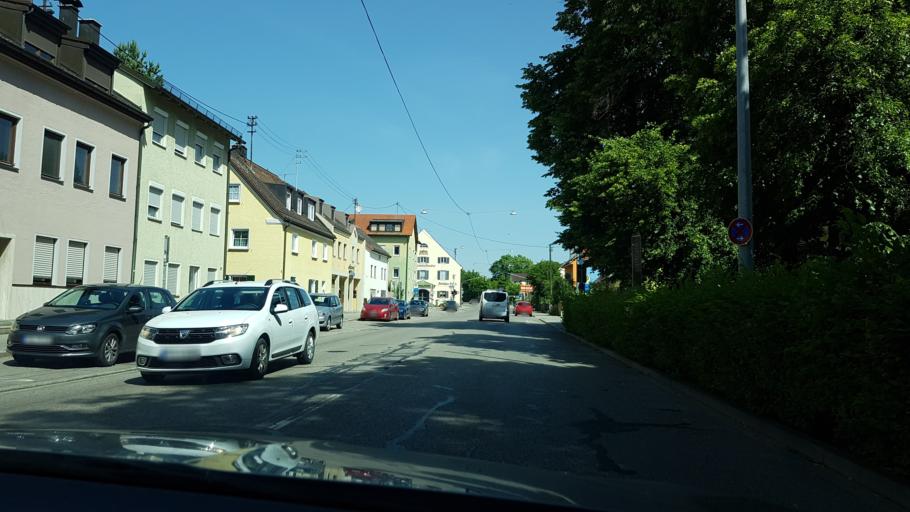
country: DE
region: Bavaria
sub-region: Upper Bavaria
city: Fuerstenfeldbruck
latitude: 48.1816
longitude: 11.2540
